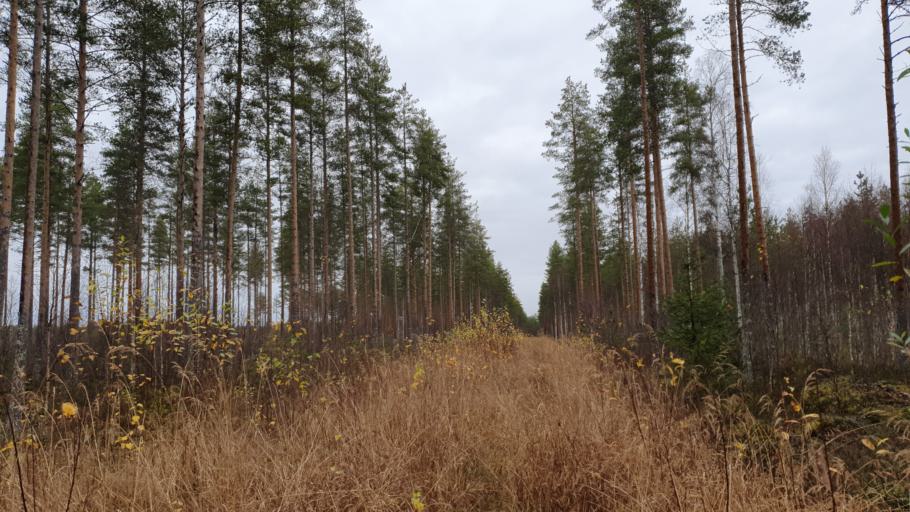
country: FI
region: Kainuu
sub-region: Kehys-Kainuu
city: Kuhmo
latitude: 64.1393
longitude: 29.4164
